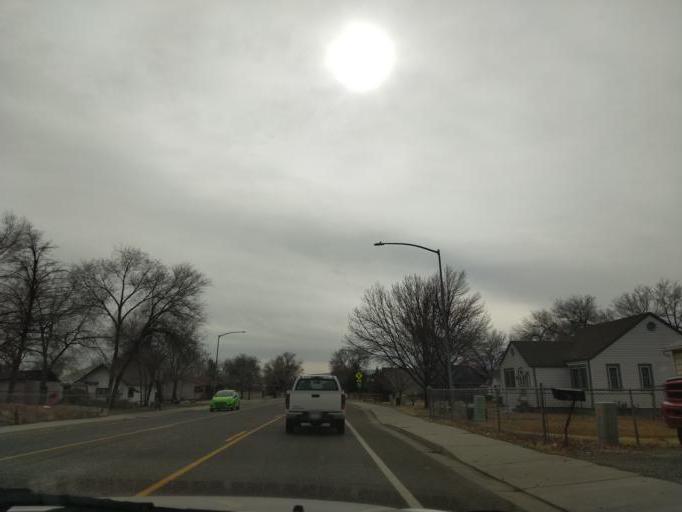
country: US
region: Colorado
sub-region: Mesa County
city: Grand Junction
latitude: 39.0818
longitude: -108.5292
